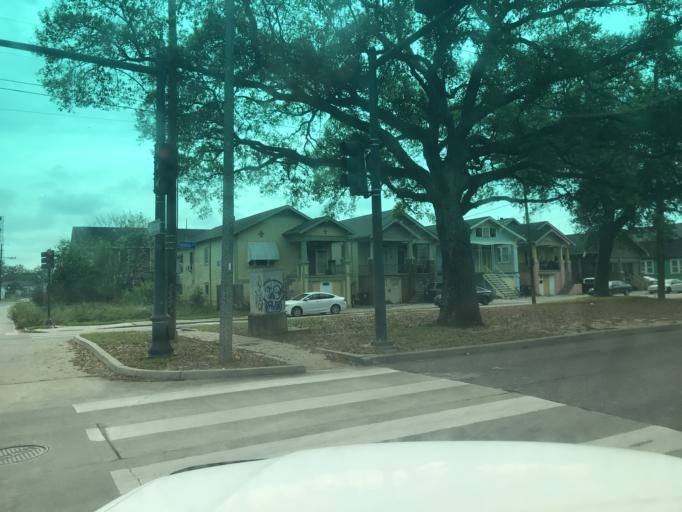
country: US
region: Louisiana
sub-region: Orleans Parish
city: New Orleans
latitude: 29.9792
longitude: -90.0486
